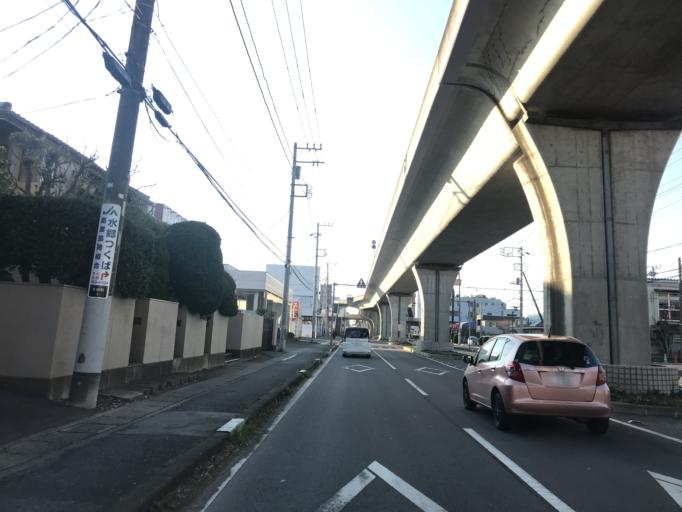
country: JP
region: Ibaraki
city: Naka
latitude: 36.0837
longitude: 140.1907
